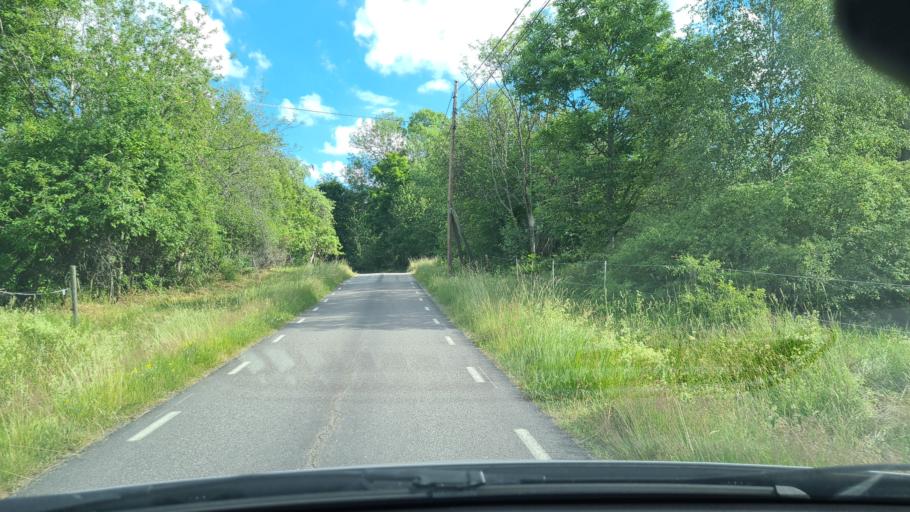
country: SE
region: Stockholm
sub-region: Vaxholms Kommun
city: Vaxholm
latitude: 59.4147
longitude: 18.4369
